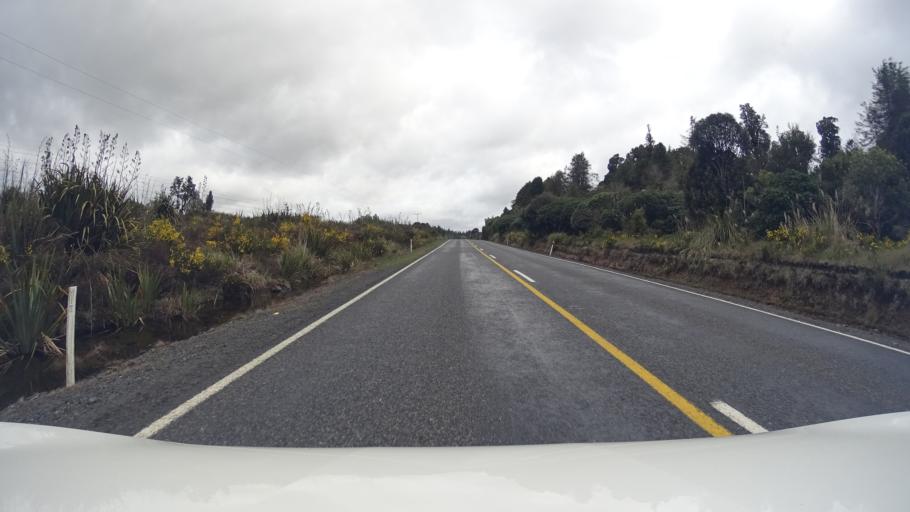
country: NZ
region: Manawatu-Wanganui
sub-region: Ruapehu District
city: Waiouru
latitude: -39.2594
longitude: 175.3888
